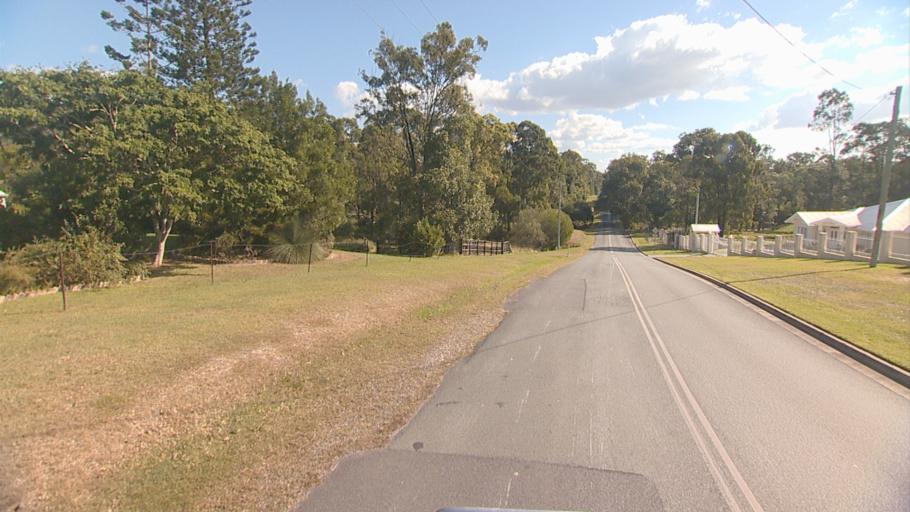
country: AU
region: Queensland
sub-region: Logan
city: Windaroo
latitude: -27.7398
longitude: 153.1730
